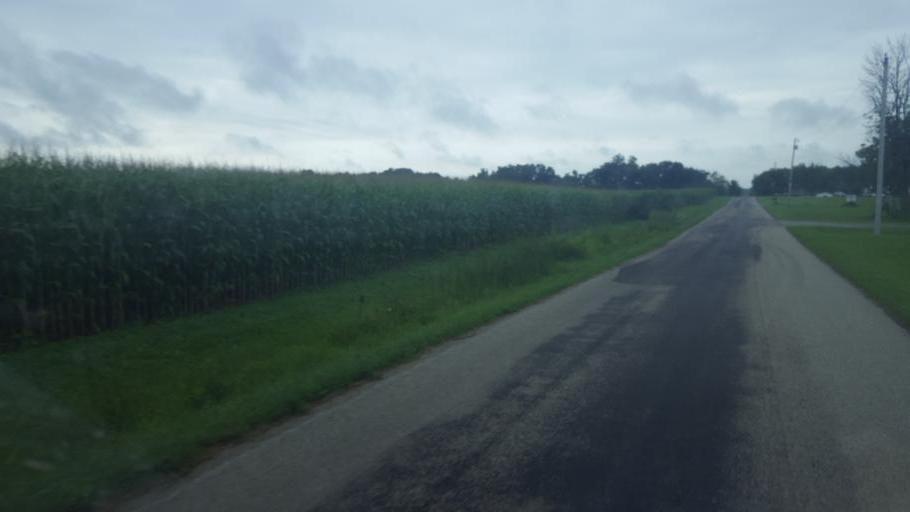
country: US
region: Ohio
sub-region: Knox County
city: Centerburg
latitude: 40.3959
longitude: -82.7409
